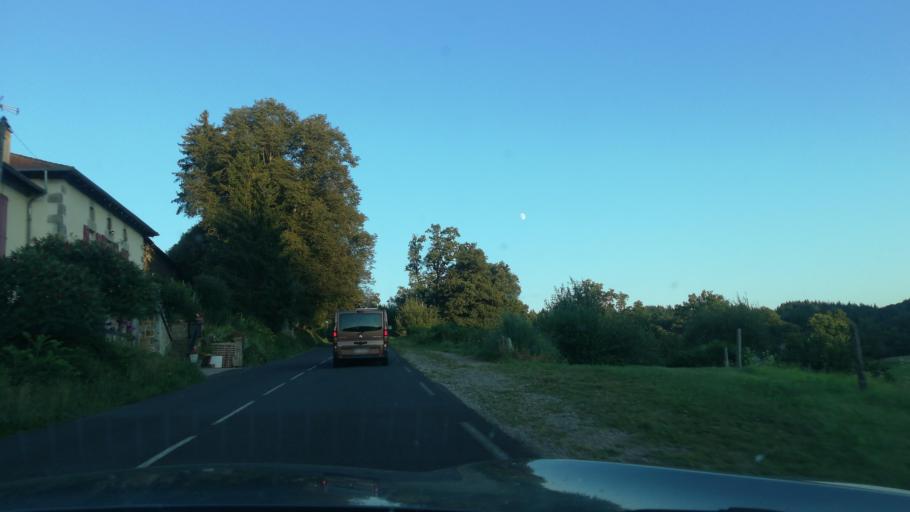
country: FR
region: Auvergne
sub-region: Departement du Cantal
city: Laroquebrou
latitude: 44.9344
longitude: 2.0781
